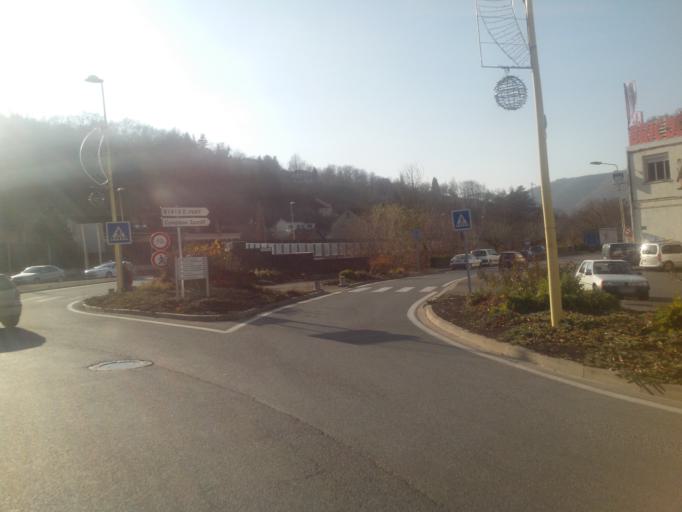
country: FR
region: Midi-Pyrenees
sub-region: Departement de l'Aveyron
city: Decazeville
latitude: 44.5628
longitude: 2.2480
